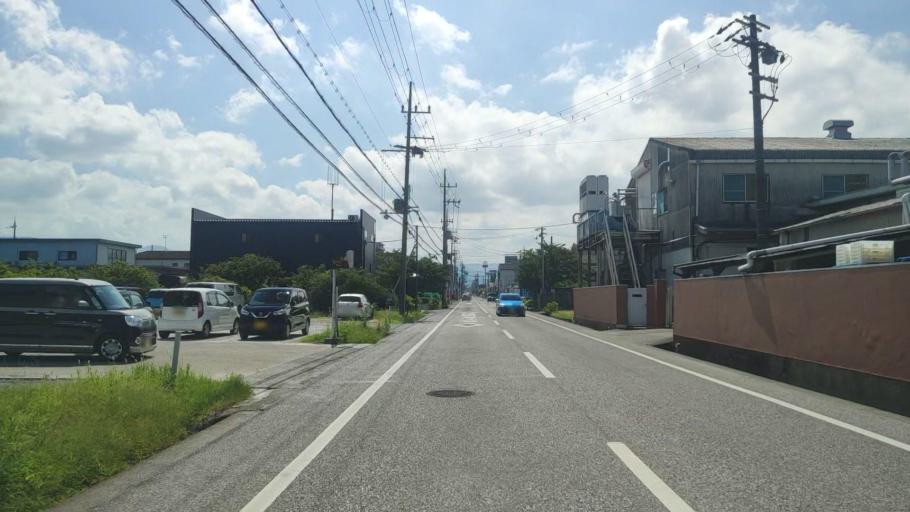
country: JP
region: Shiga Prefecture
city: Hikone
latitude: 35.2622
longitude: 136.2363
